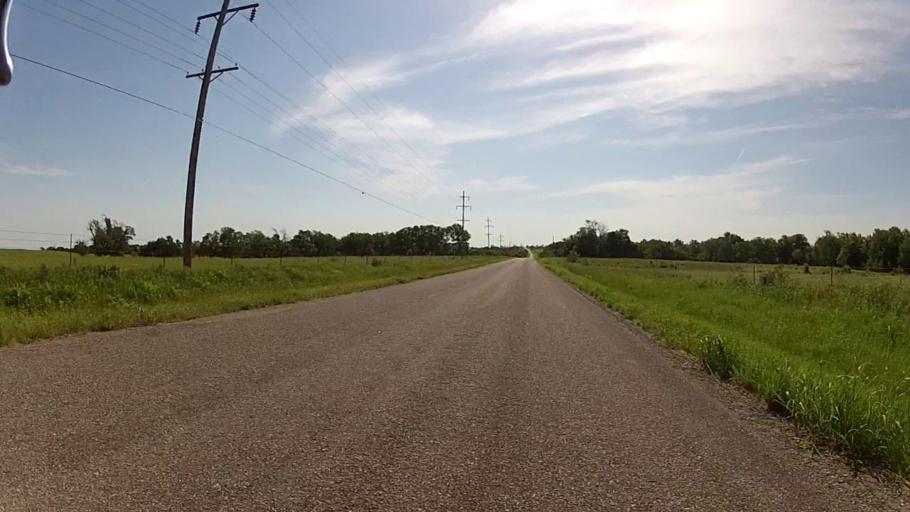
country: US
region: Kansas
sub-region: Cowley County
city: Winfield
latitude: 37.0711
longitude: -96.6704
